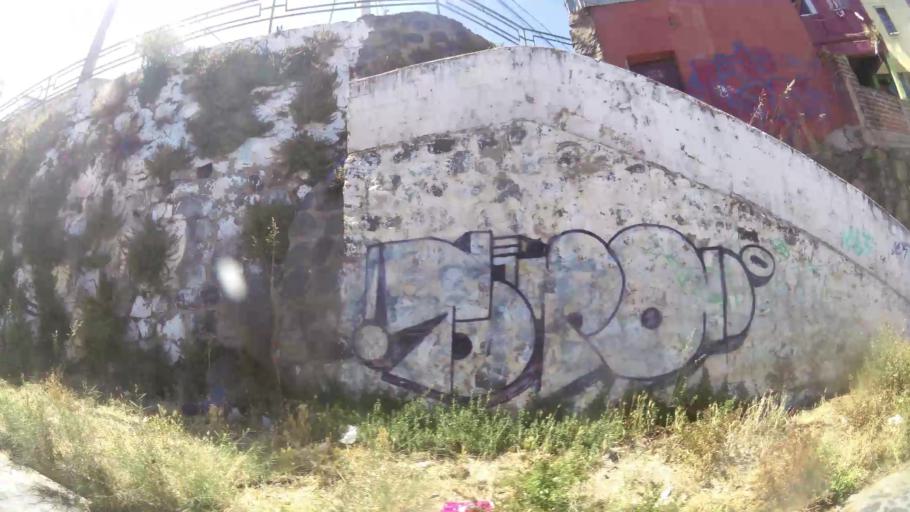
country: CL
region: Valparaiso
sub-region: Provincia de Valparaiso
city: Valparaiso
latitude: -33.0515
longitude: -71.5991
